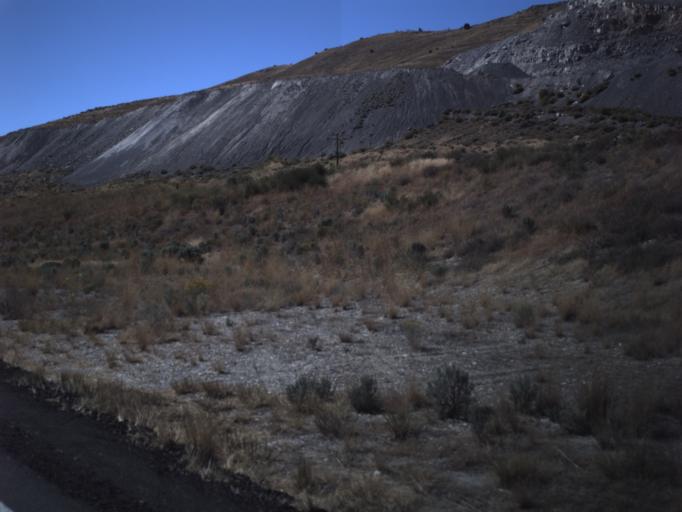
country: US
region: Utah
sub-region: Utah County
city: Saratoga Springs
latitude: 40.2561
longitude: -111.8671
